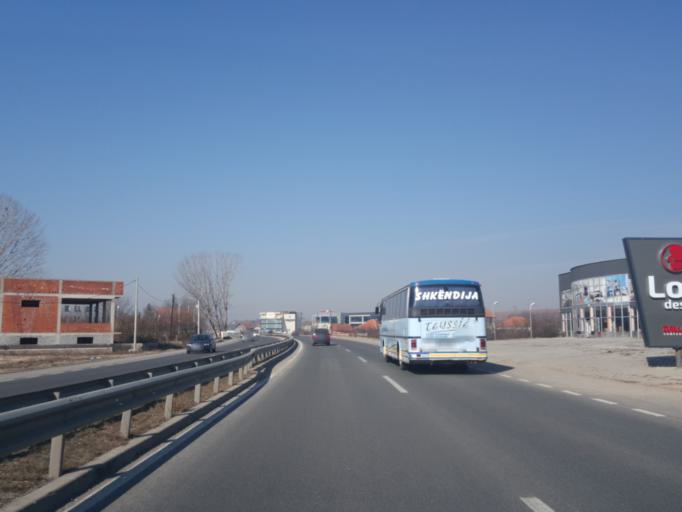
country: XK
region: Pristina
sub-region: Komuna e Obiliqit
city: Obiliq
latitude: 42.7324
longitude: 21.0720
